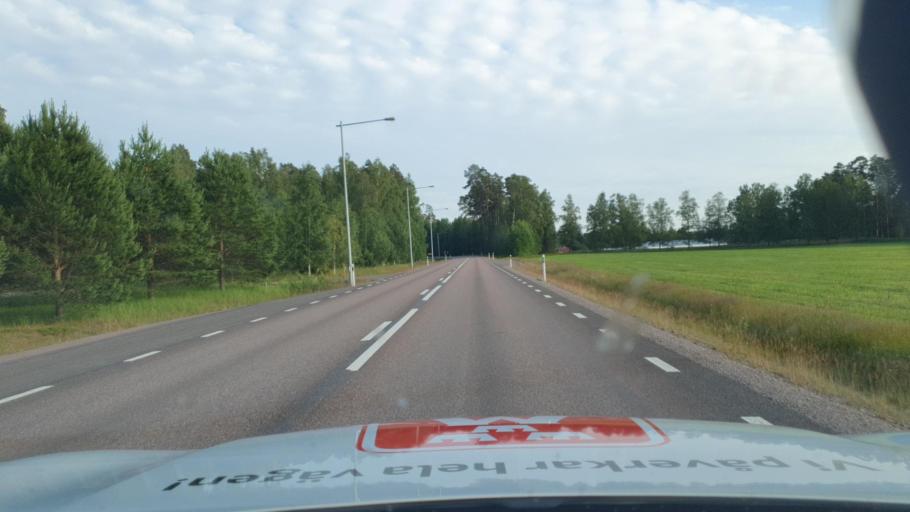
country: SE
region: Vaermland
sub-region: Hagfors Kommun
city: Hagfors
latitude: 59.9978
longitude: 13.6422
